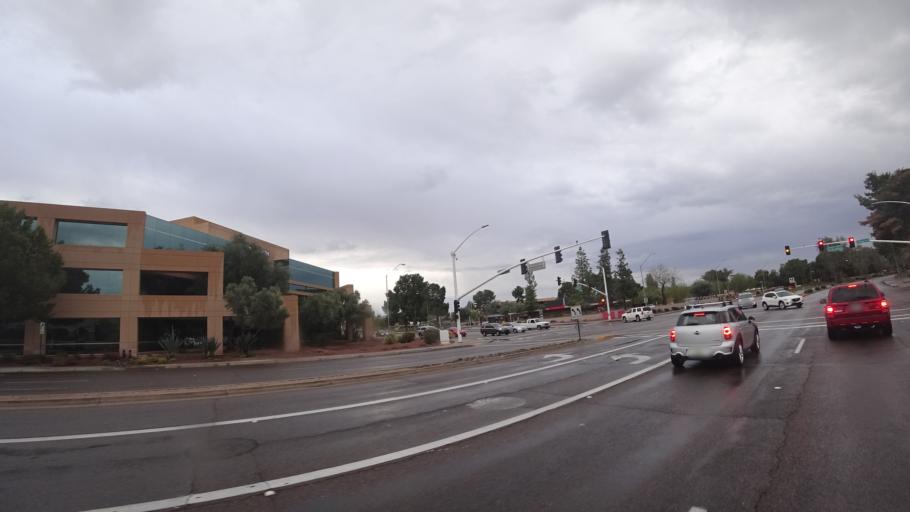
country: US
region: Arizona
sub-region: Maricopa County
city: Scottsdale
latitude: 33.5548
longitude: -111.8987
